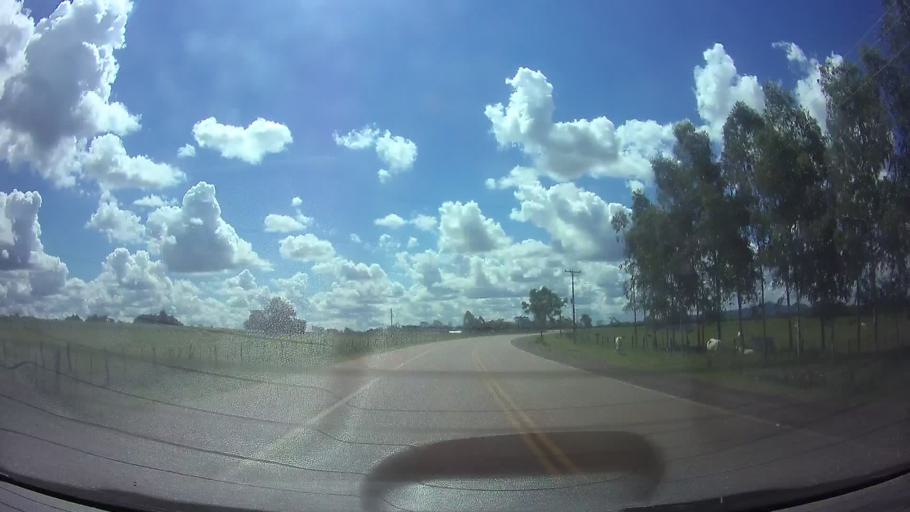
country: PY
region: Paraguari
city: La Colmena
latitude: -25.9105
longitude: -56.7577
